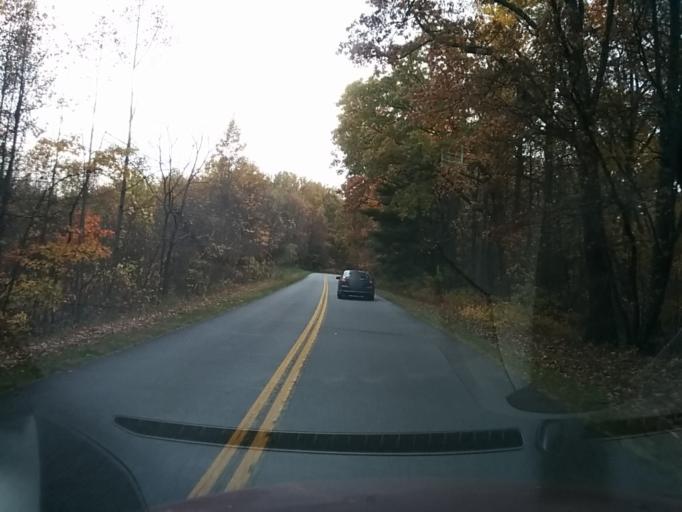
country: US
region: Virginia
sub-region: City of Buena Vista
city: Buena Vista
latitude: 37.8120
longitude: -79.2340
